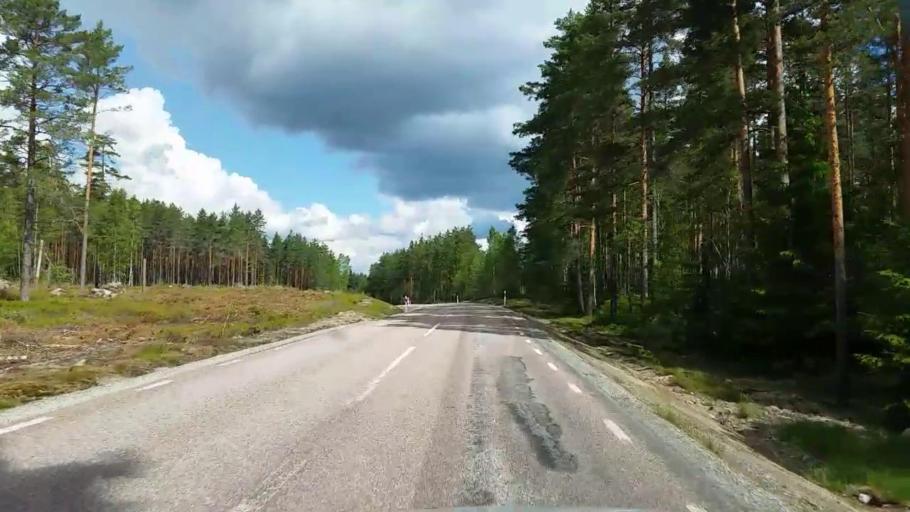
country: SE
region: Vaestmanland
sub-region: Skinnskattebergs Kommun
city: Skinnskatteberg
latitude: 59.8070
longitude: 15.8419
